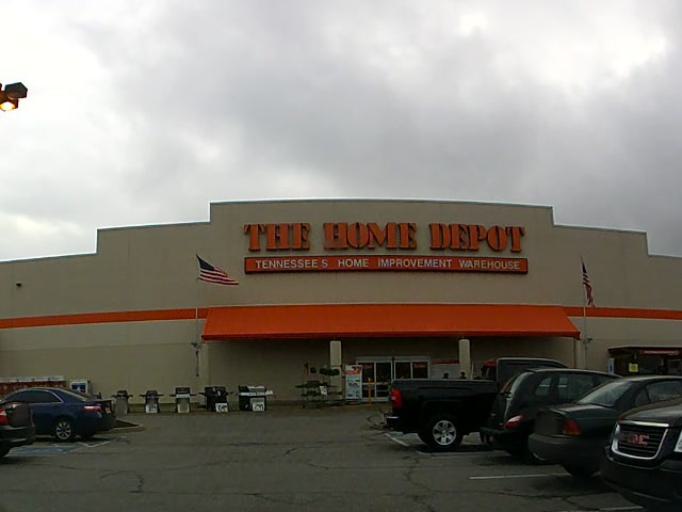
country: US
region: Tennessee
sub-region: Shelby County
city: Germantown
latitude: 35.1096
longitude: -89.8926
